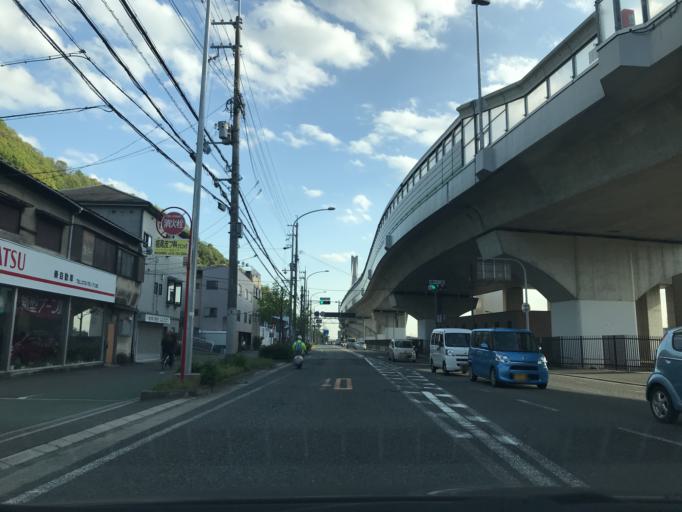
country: JP
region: Osaka
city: Ikeda
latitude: 34.8370
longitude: 135.4263
